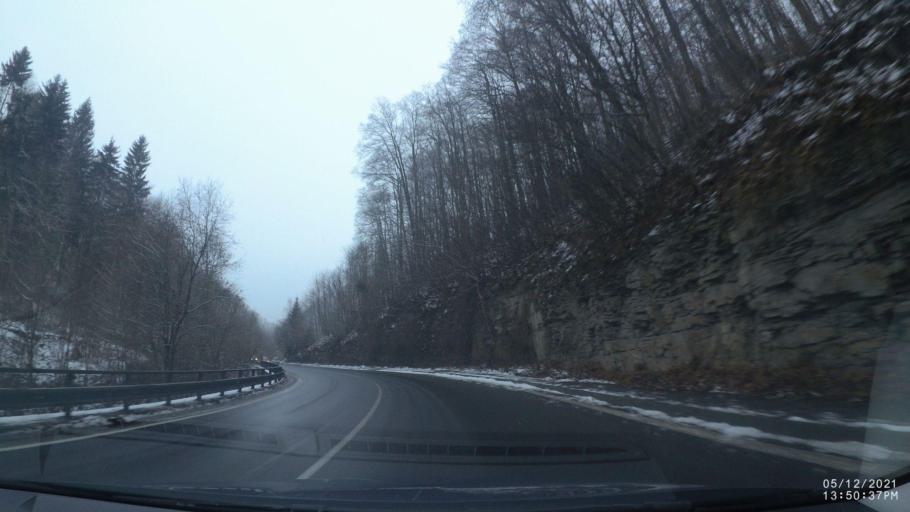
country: CZ
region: Kralovehradecky
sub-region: Okres Nachod
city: Police nad Metuji
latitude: 50.5348
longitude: 16.2272
